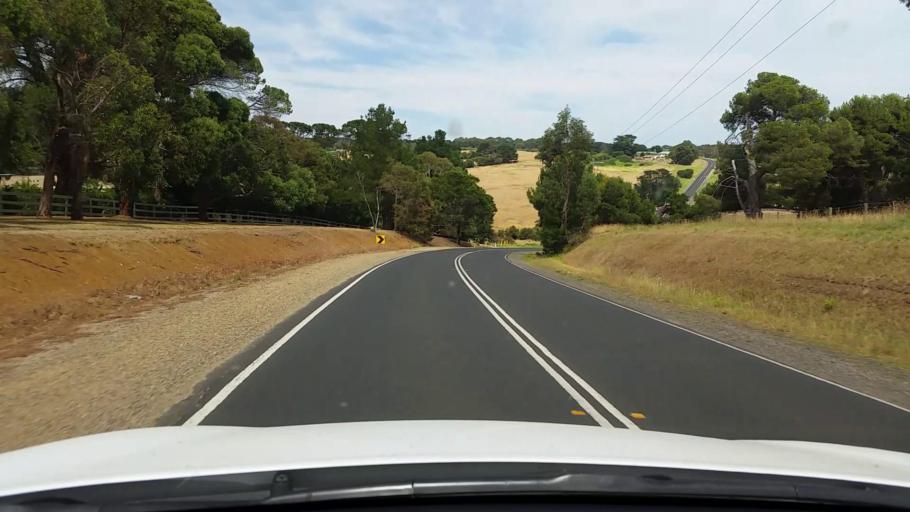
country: AU
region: Victoria
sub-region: Mornington Peninsula
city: Merricks
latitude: -38.4485
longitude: 145.0310
